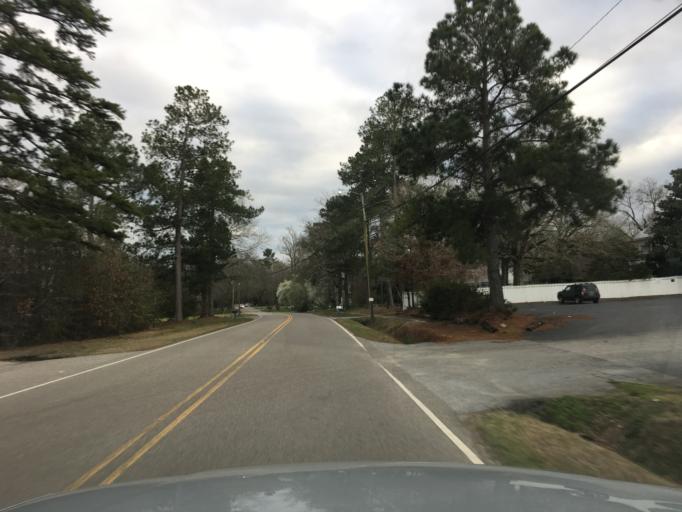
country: US
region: South Carolina
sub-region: Saluda County
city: Saluda
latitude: 33.9992
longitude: -81.7732
